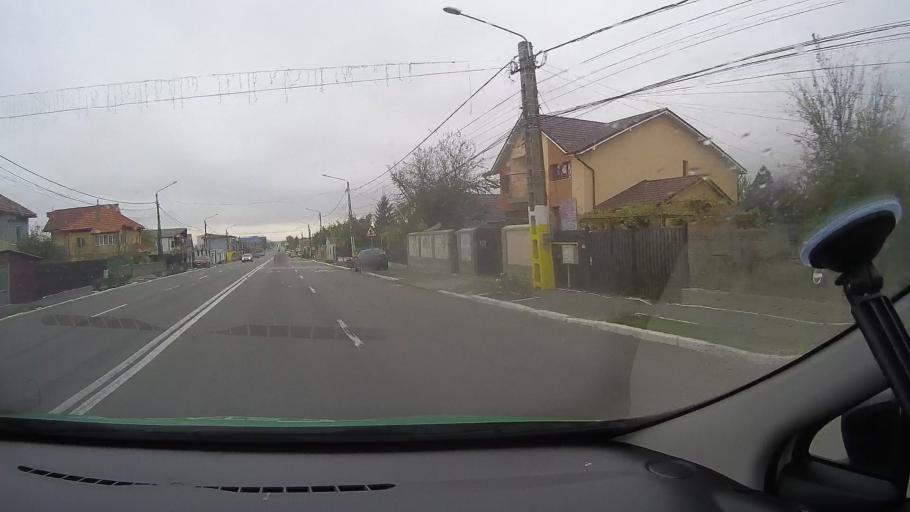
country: RO
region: Constanta
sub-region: Comuna Valu lui Traian
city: Valu lui Traian
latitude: 44.1650
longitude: 28.4699
